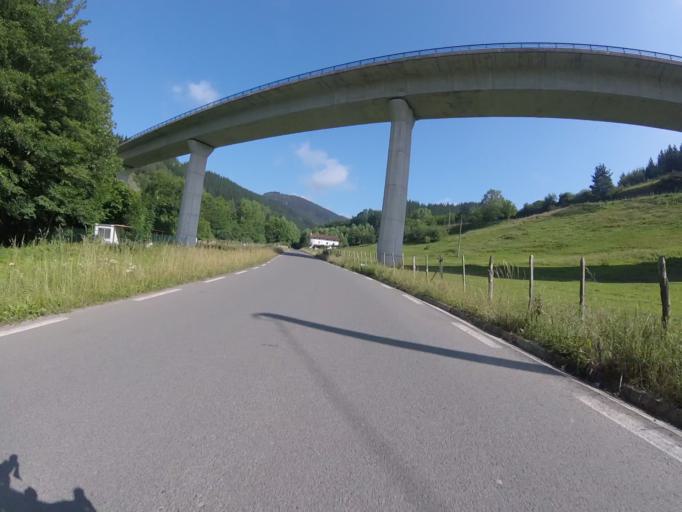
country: ES
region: Basque Country
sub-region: Provincia de Guipuzcoa
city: Ormaiztegui
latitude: 43.0537
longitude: -2.2342
